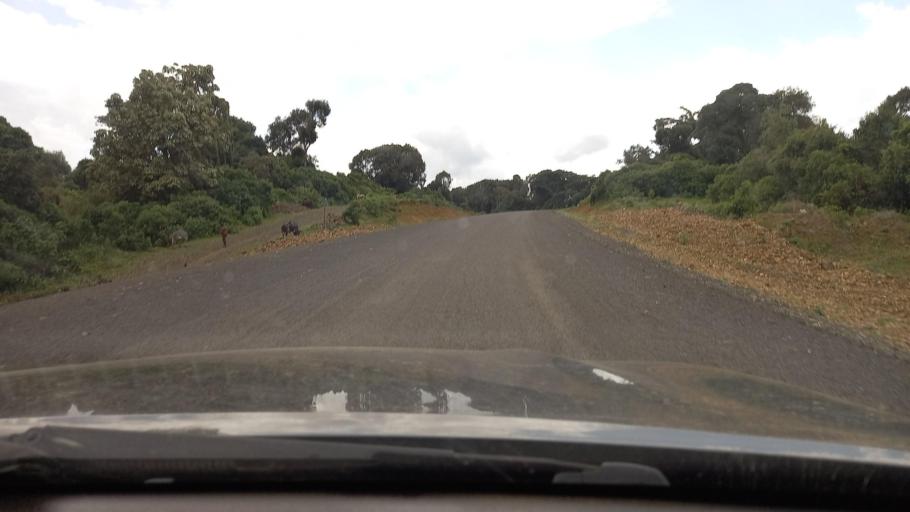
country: ET
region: Southern Nations, Nationalities, and People's Region
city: Mizan Teferi
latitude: 6.2092
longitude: 35.6117
